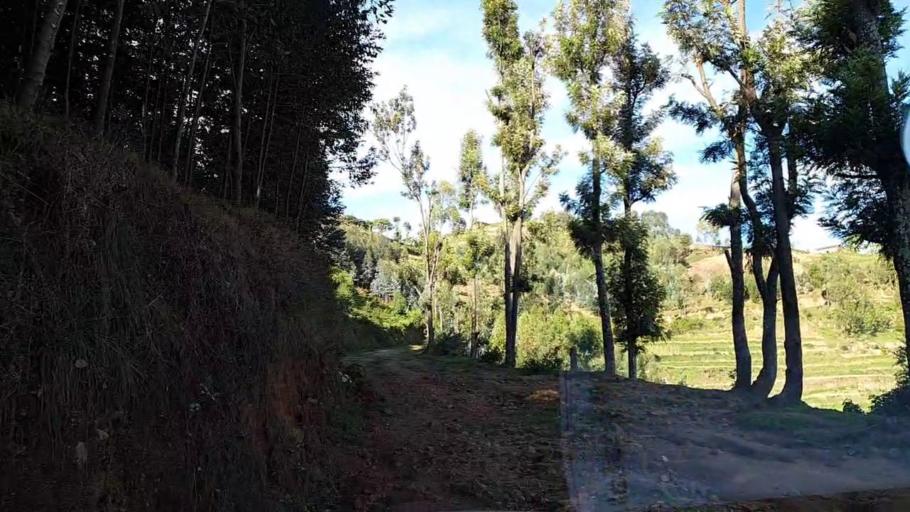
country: RW
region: Southern Province
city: Nzega
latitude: -2.4144
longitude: 29.5159
